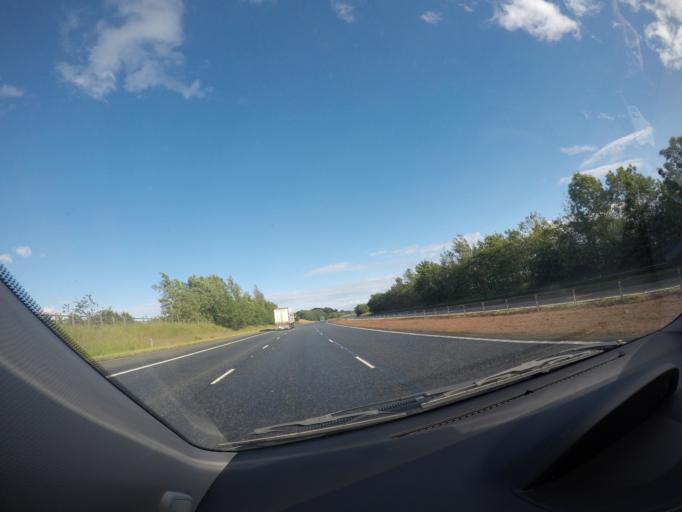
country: GB
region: Scotland
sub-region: Dumfries and Galloway
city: Annan
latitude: 55.0421
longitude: -3.1822
